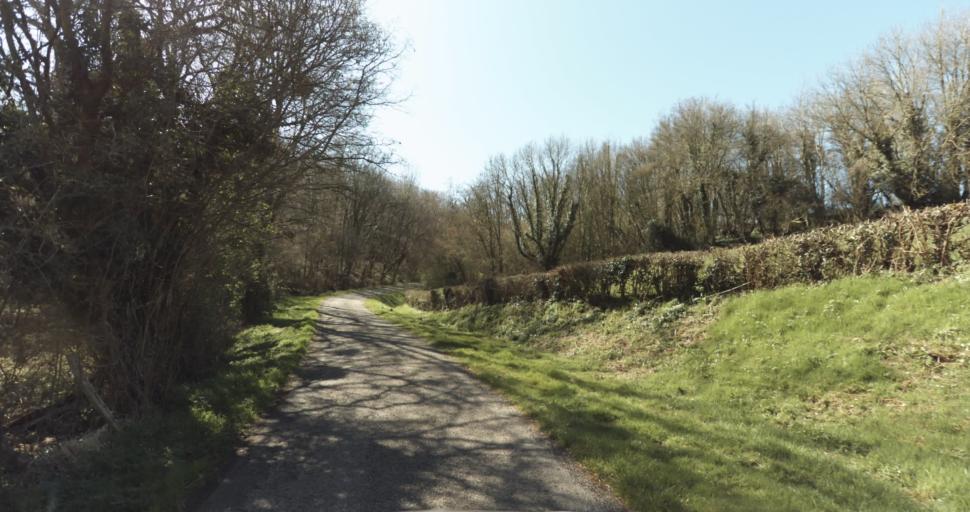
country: FR
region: Lower Normandy
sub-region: Departement de l'Orne
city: Trun
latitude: 48.9372
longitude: 0.0715
